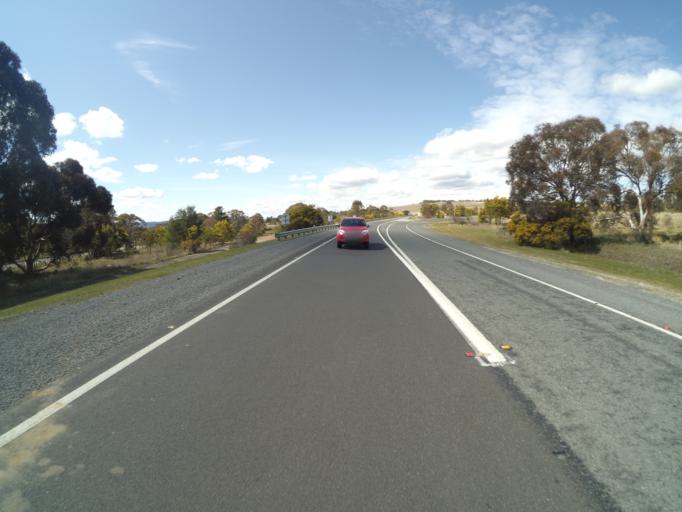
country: AU
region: New South Wales
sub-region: Goulburn Mulwaree
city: Goulburn
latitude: -34.7423
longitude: 149.7688
